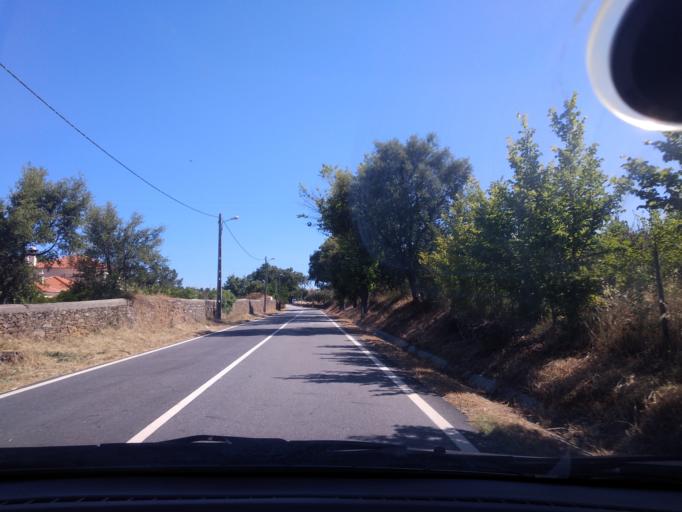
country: PT
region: Castelo Branco
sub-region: Castelo Branco
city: Castelo Branco
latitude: 39.7449
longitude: -7.6208
